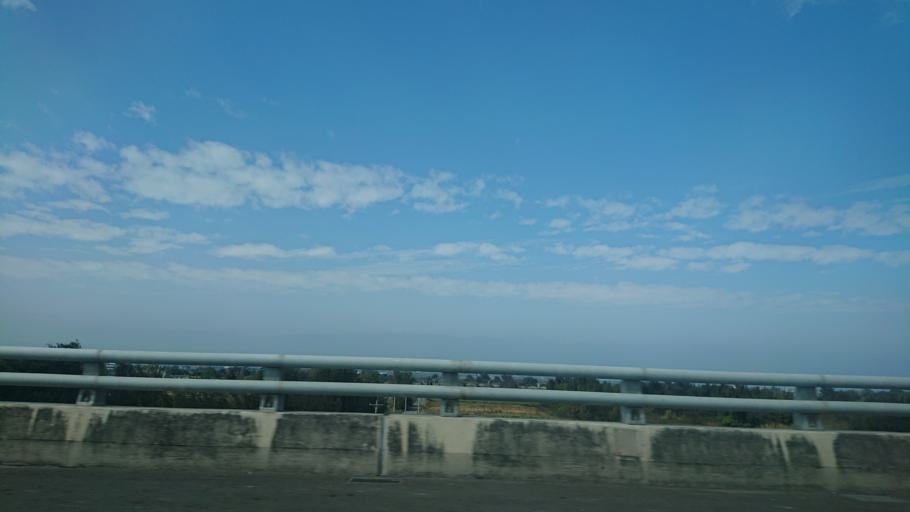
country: TW
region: Taiwan
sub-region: Yunlin
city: Douliu
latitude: 23.8511
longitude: 120.2952
